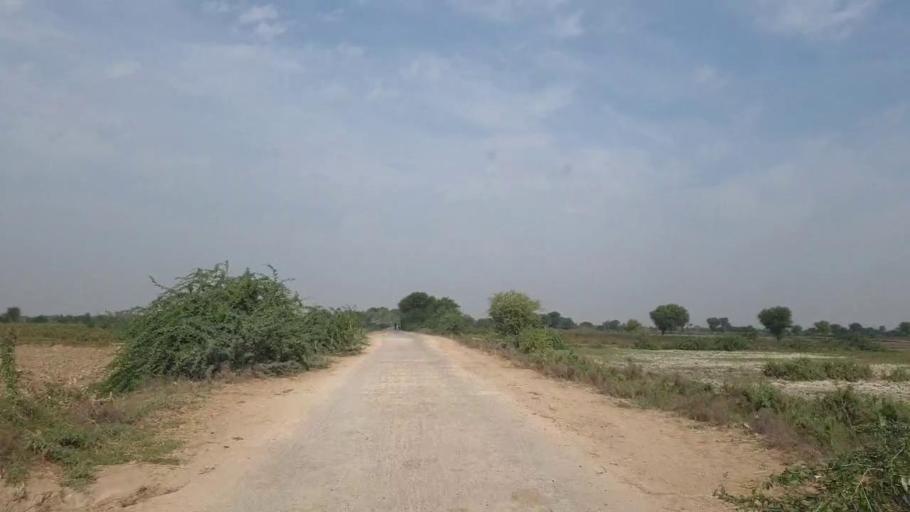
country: PK
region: Sindh
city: Rajo Khanani
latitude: 24.9338
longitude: 68.9875
